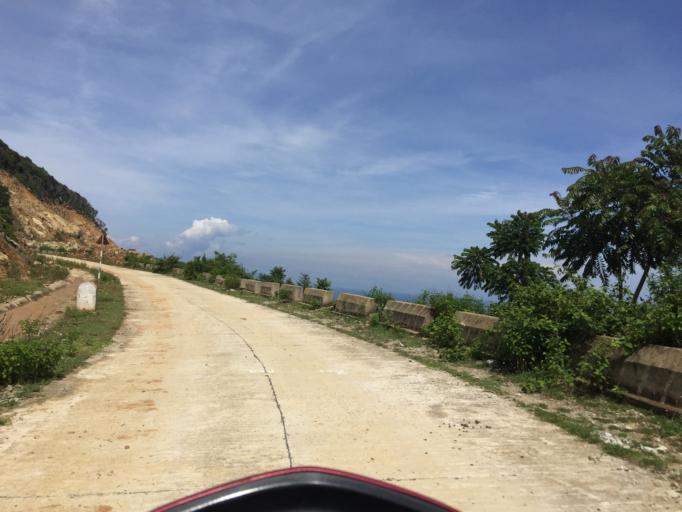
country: VN
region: Quang Nam
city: Hoi An
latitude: 15.9742
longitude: 108.5075
